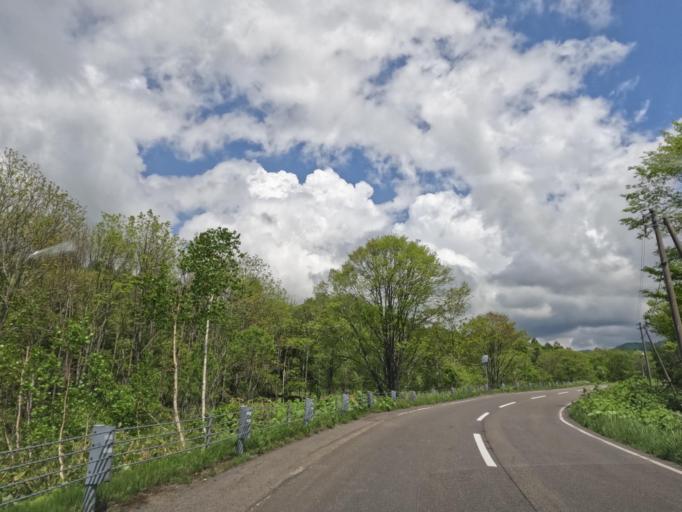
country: JP
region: Hokkaido
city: Takikawa
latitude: 43.5431
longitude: 141.6404
